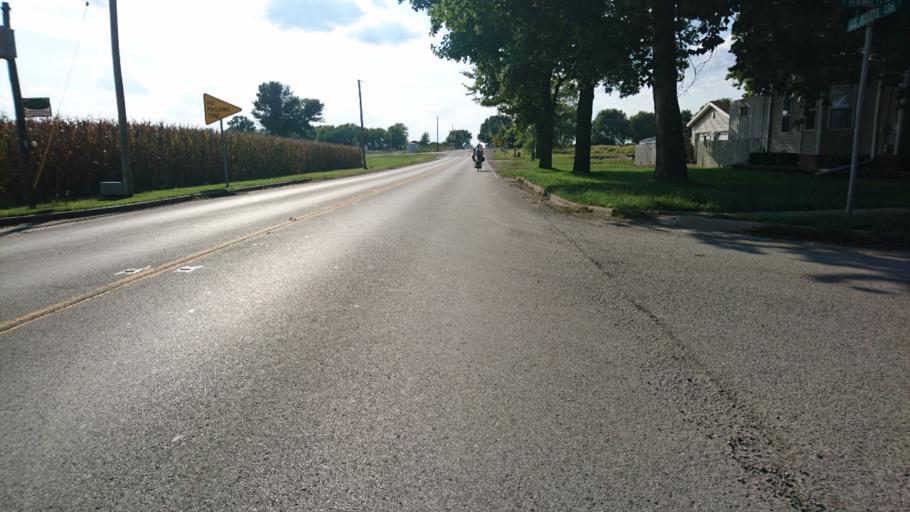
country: US
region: Illinois
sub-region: Logan County
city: Atlanta
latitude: 40.3116
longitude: -89.1709
